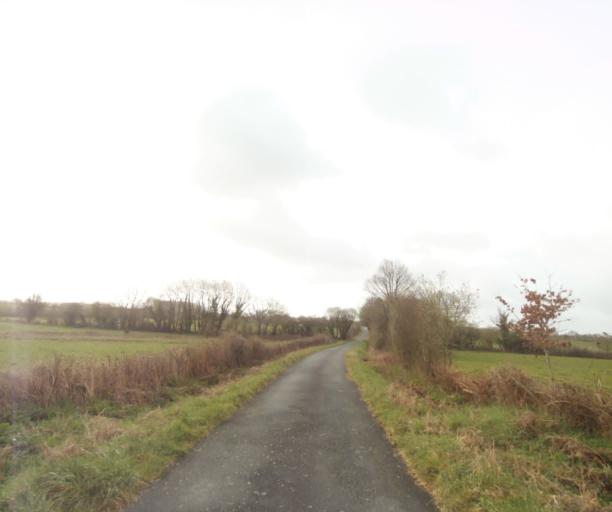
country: FR
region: Pays de la Loire
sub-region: Departement de la Loire-Atlantique
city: Bouvron
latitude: 47.4057
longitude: -1.8741
